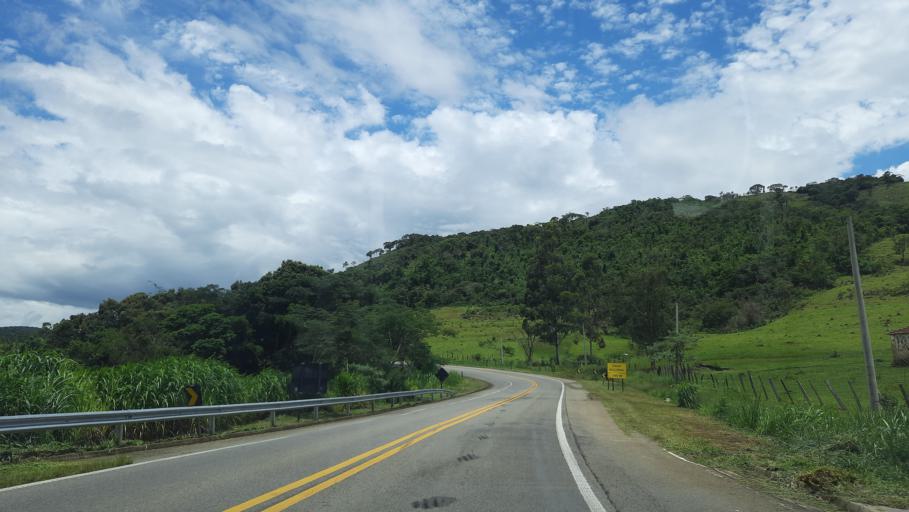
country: BR
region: Sao Paulo
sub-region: Vargem Grande Do Sul
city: Vargem Grande do Sul
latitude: -21.8269
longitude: -46.7748
